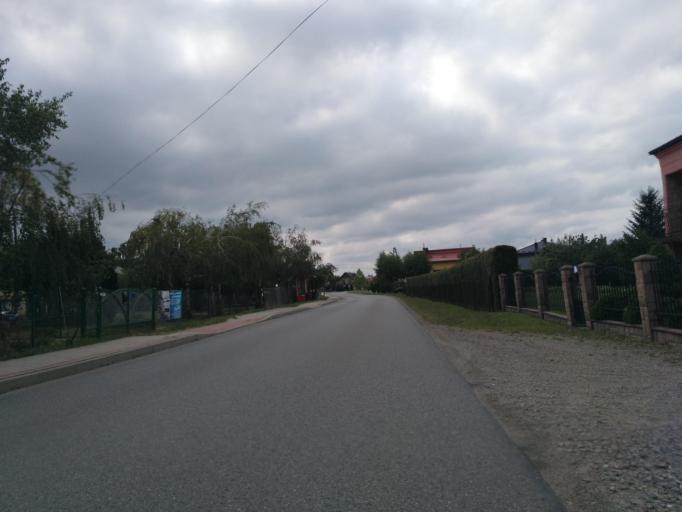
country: PL
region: Subcarpathian Voivodeship
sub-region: Powiat krosnienski
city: Kroscienko Wyzne
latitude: 49.6463
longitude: 21.8213
